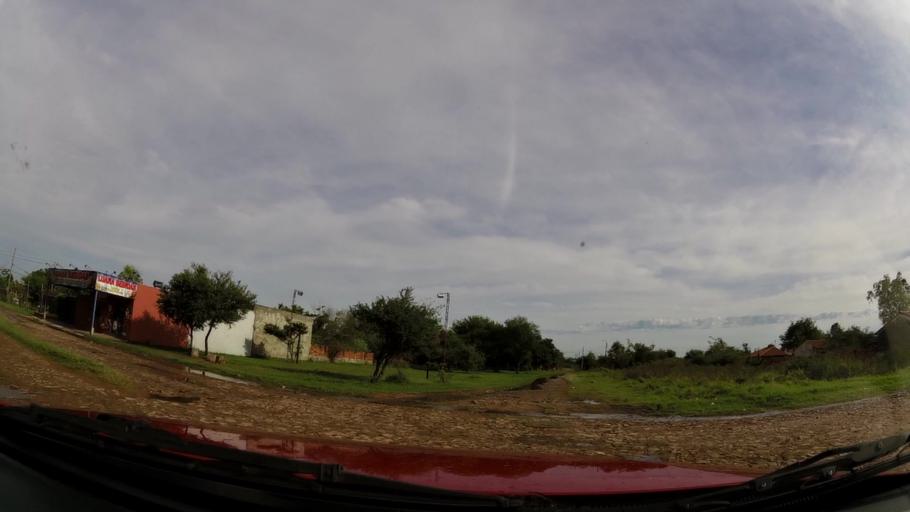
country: PY
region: Central
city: Limpio
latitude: -25.1667
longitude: -57.4841
